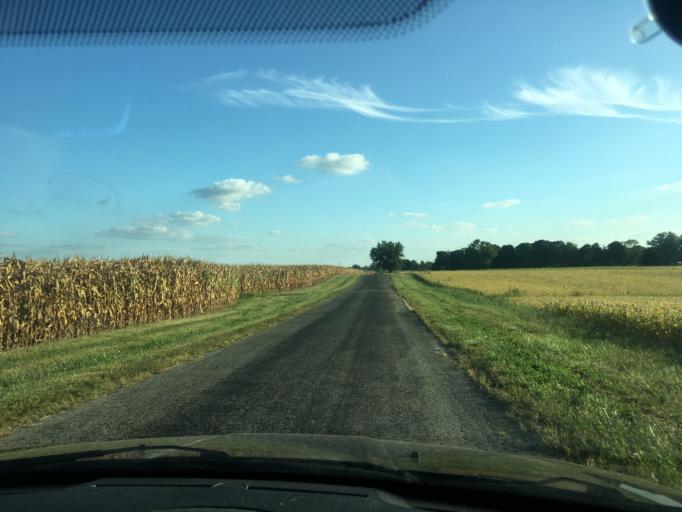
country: US
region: Ohio
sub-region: Logan County
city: West Liberty
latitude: 40.2130
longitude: -83.7398
